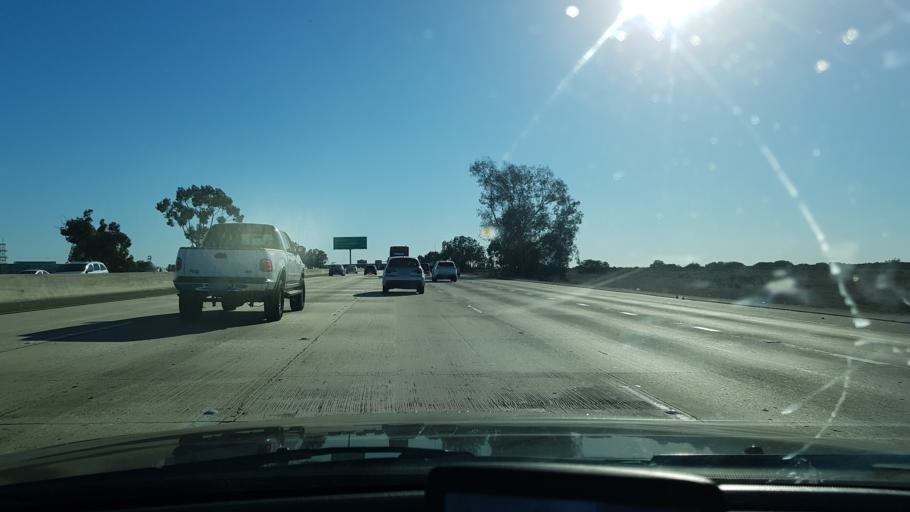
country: US
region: California
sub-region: San Diego County
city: La Mesa
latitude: 32.8474
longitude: -117.1280
